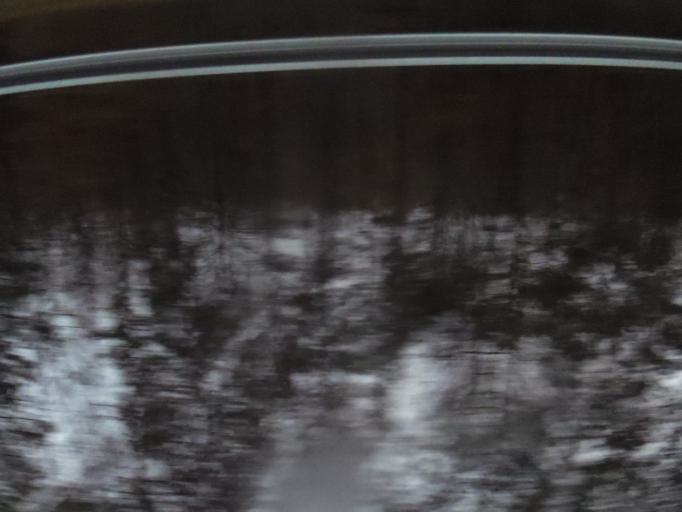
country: US
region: Alabama
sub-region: Cullman County
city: Cullman
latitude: 34.1978
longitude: -86.8784
